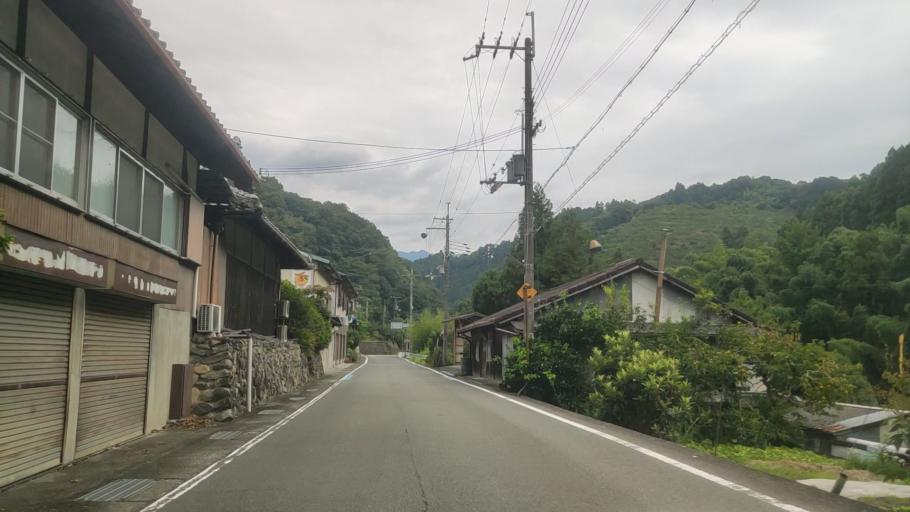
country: JP
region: Wakayama
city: Hashimoto
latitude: 34.2821
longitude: 135.5617
